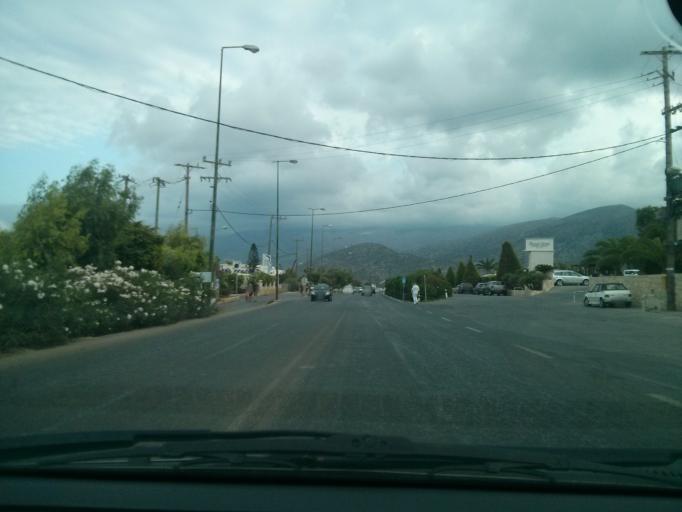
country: GR
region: Crete
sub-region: Nomos Irakleiou
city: Stalis
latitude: 35.3026
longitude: 25.4192
